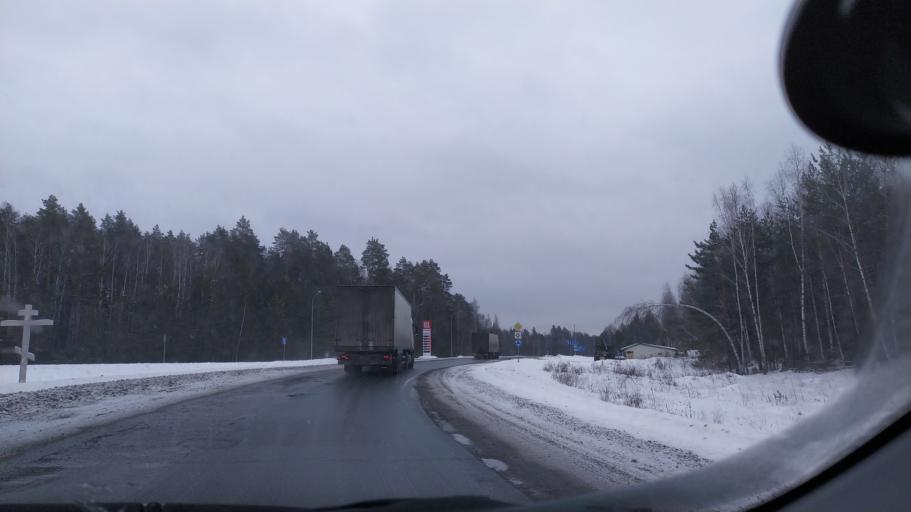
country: RU
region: Chuvashia
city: Mariinskiy Posad
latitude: 56.1889
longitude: 47.7849
